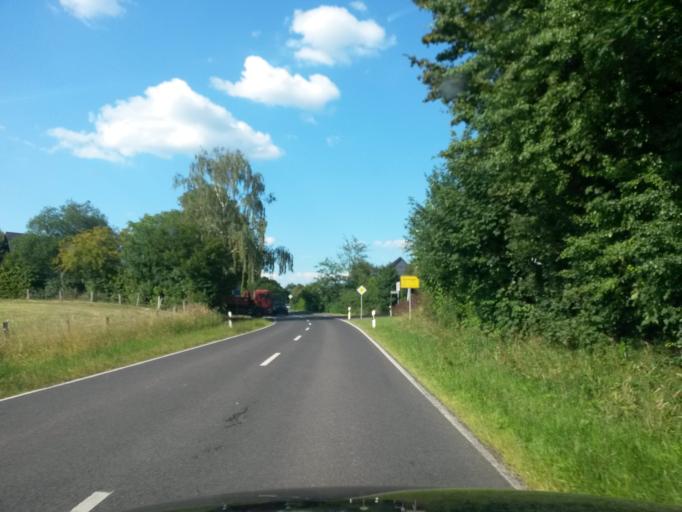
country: DE
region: North Rhine-Westphalia
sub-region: Regierungsbezirk Koln
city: Much
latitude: 50.9156
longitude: 7.3753
